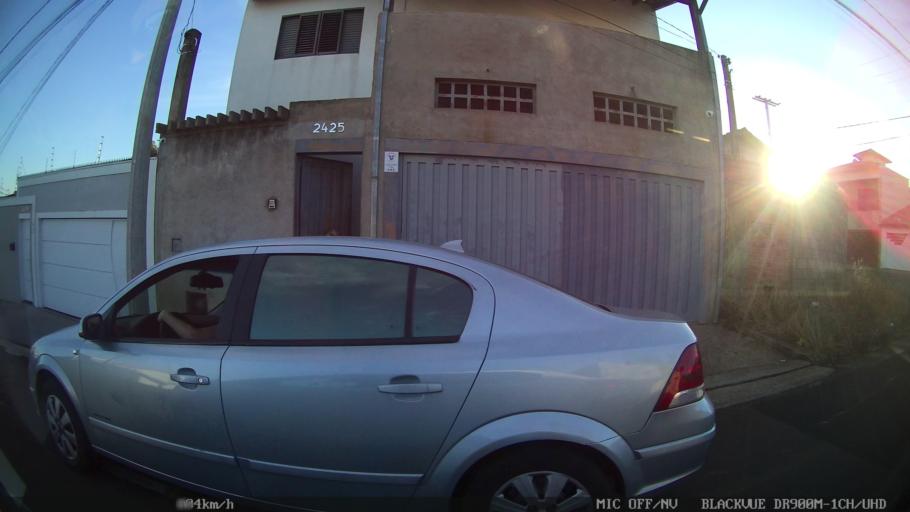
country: BR
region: Sao Paulo
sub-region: Franca
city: Franca
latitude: -20.5111
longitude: -47.3969
